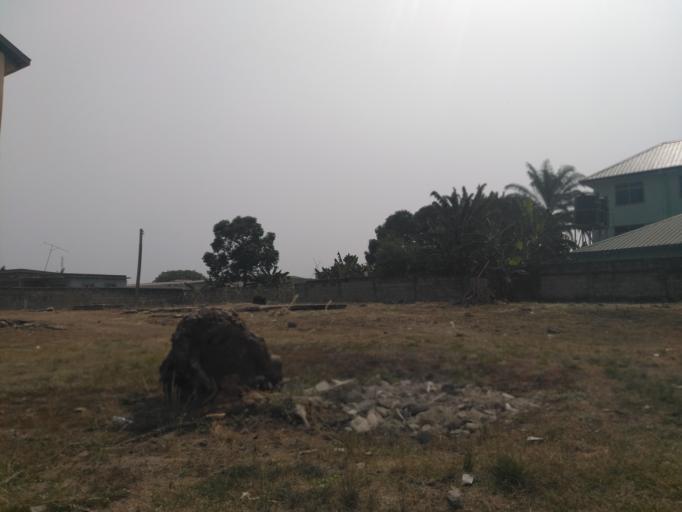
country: GH
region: Ashanti
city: Kumasi
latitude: 6.6788
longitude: -1.6007
